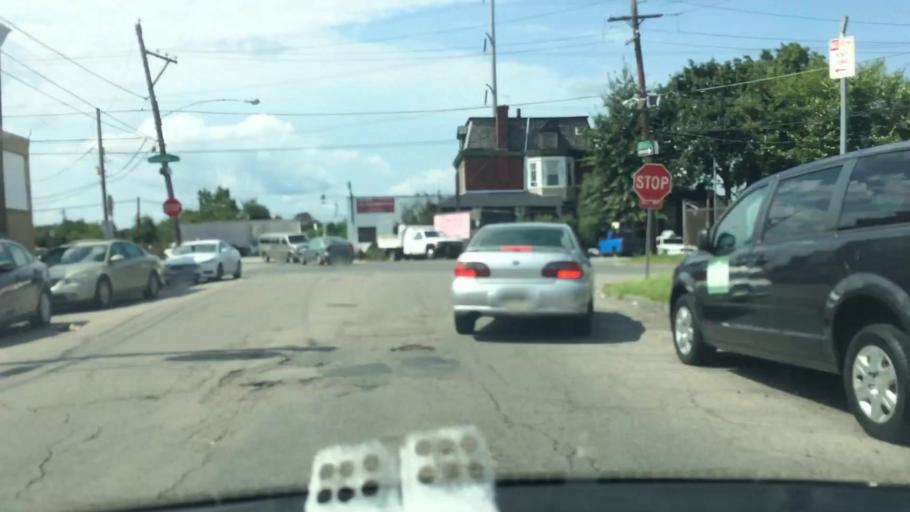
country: US
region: Pennsylvania
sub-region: Delaware County
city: Yeadon
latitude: 39.9282
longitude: -75.2326
